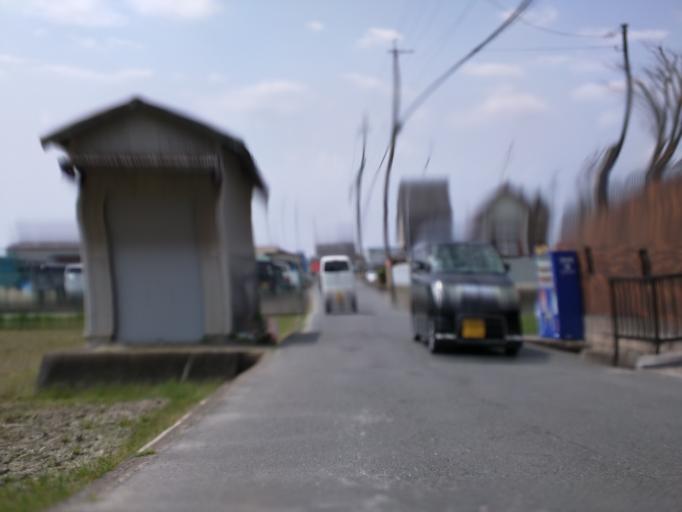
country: JP
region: Kyoto
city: Tanabe
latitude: 34.7982
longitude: 135.7939
